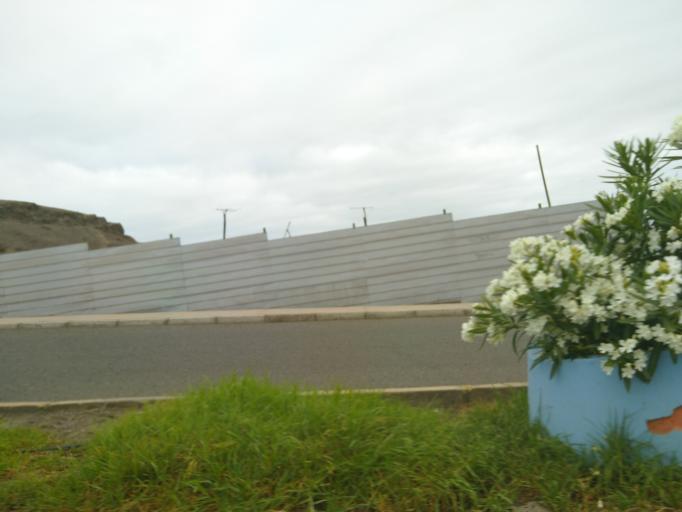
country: CL
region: Antofagasta
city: Taltal
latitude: -25.4039
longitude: -70.4795
